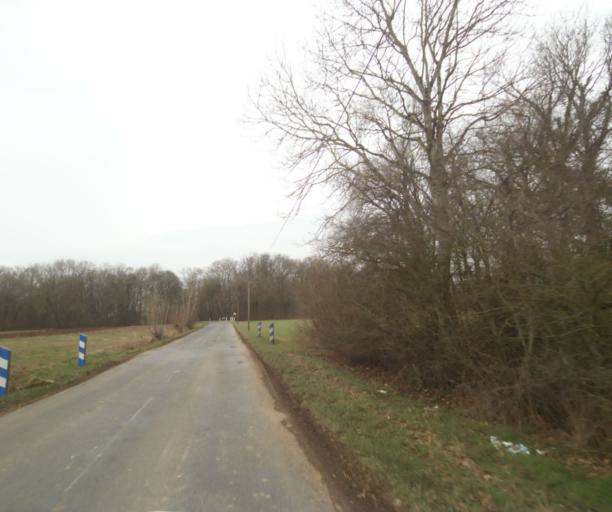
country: FR
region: Champagne-Ardenne
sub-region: Departement de la Haute-Marne
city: Villiers-en-Lieu
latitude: 48.6588
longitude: 4.8799
